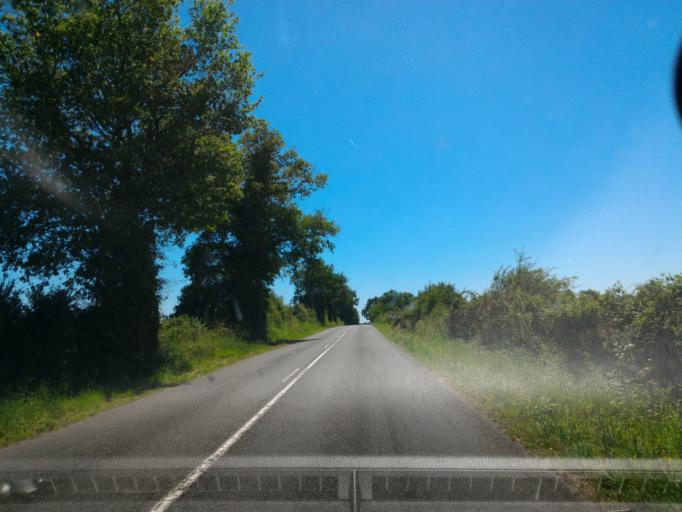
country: FR
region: Poitou-Charentes
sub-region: Departement de la Vienne
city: Availles-Limouzine
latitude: 46.2046
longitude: 0.7058
